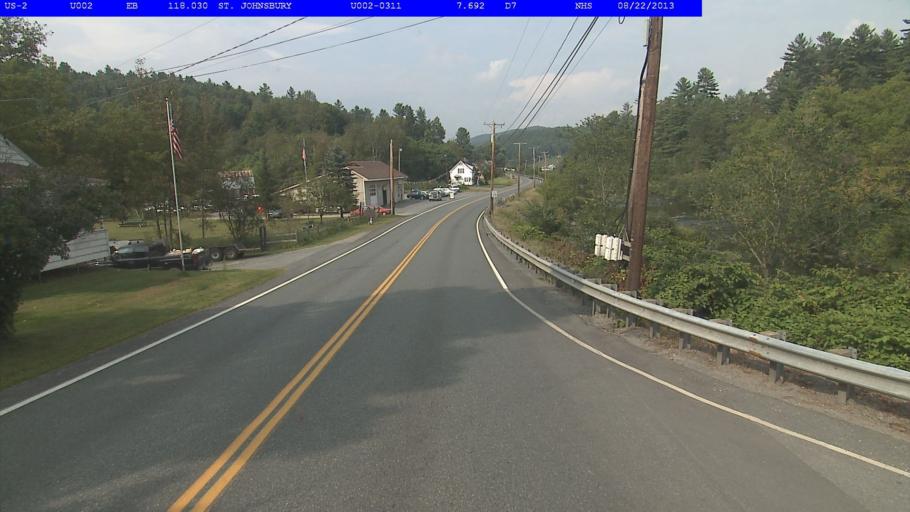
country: US
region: Vermont
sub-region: Caledonia County
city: St Johnsbury
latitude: 44.4391
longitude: -71.9466
